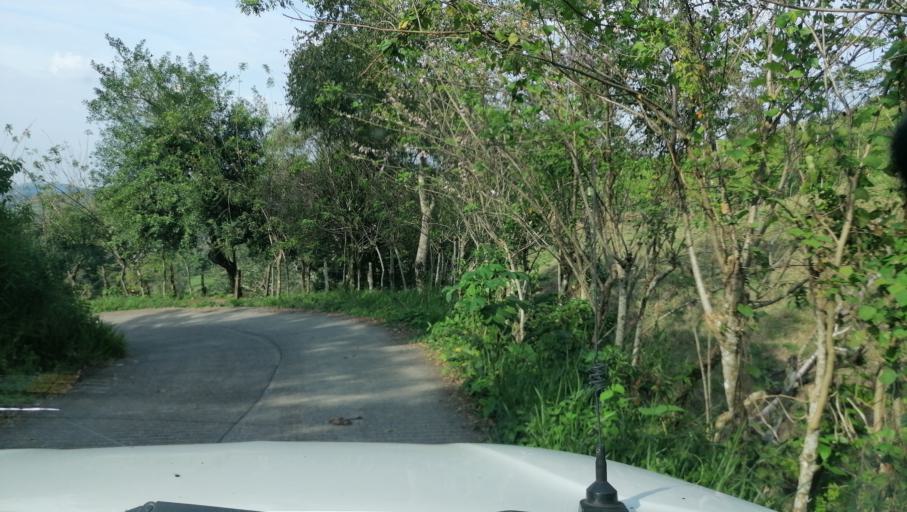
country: MX
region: Chiapas
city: Ostuacan
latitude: 17.4808
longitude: -93.2390
